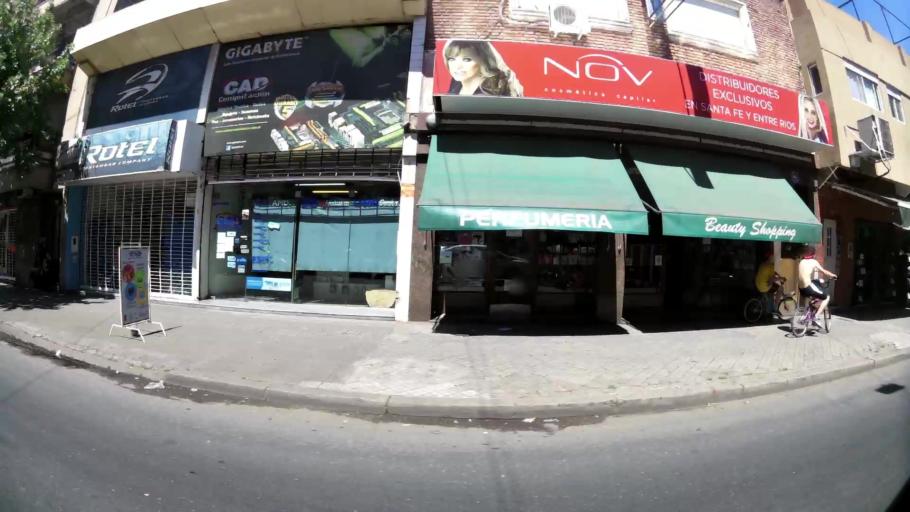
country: AR
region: Santa Fe
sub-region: Departamento de Rosario
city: Rosario
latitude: -32.9387
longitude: -60.6704
